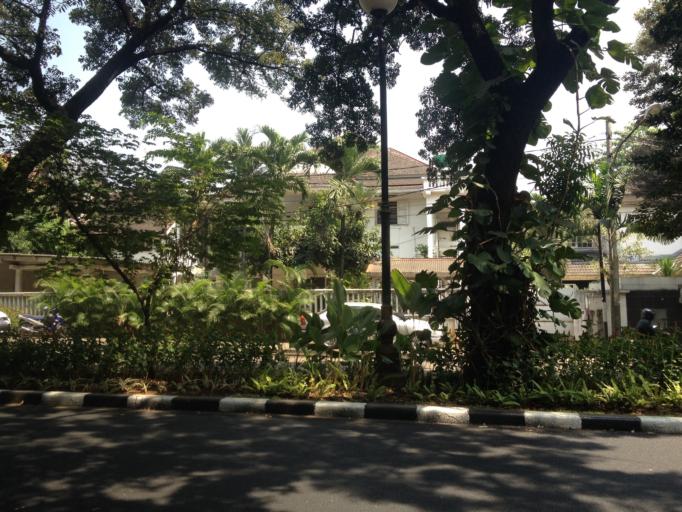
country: ID
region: Jakarta Raya
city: Jakarta
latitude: -6.1969
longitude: 106.8331
